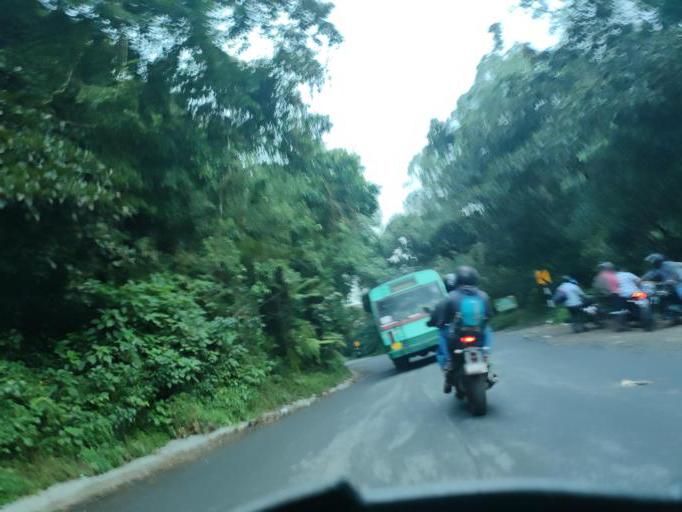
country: IN
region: Tamil Nadu
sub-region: Dindigul
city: Kodaikanal
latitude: 10.2475
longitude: 77.5189
